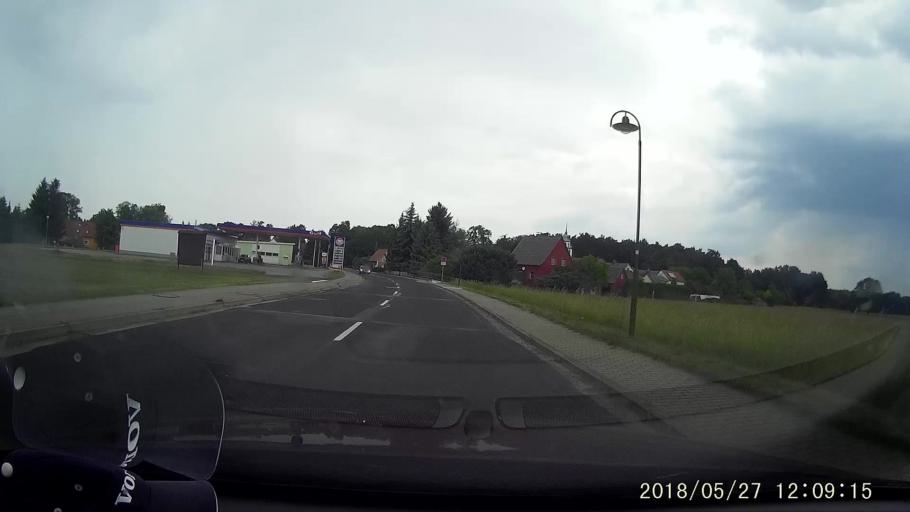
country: DE
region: Saxony
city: Klitten
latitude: 51.3501
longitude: 14.6004
